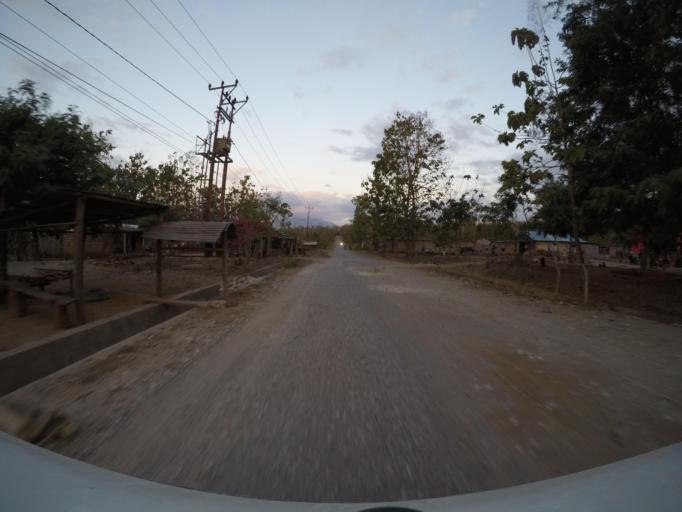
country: TL
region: Bobonaro
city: Maliana
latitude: -8.9621
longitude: 125.1202
